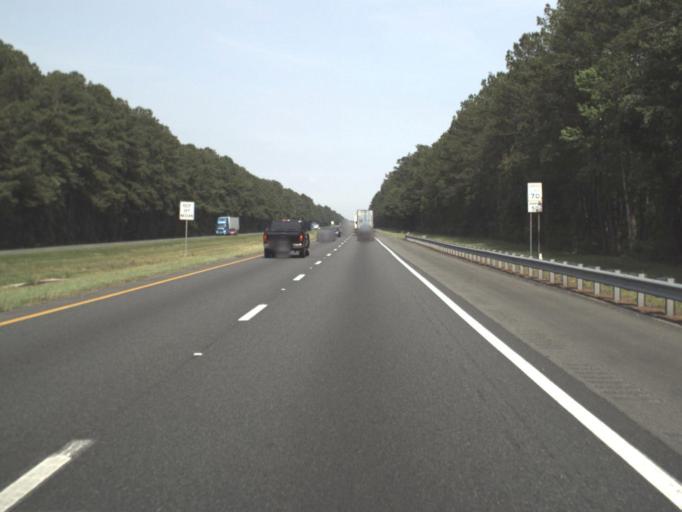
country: US
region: Florida
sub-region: Baker County
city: Macclenny
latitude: 30.2609
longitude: -82.1534
